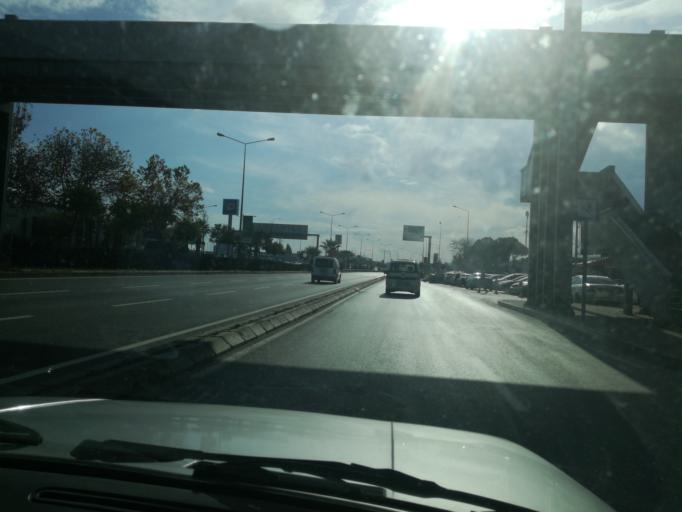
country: TR
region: Izmir
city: Karabaglar
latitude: 38.3521
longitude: 27.1335
